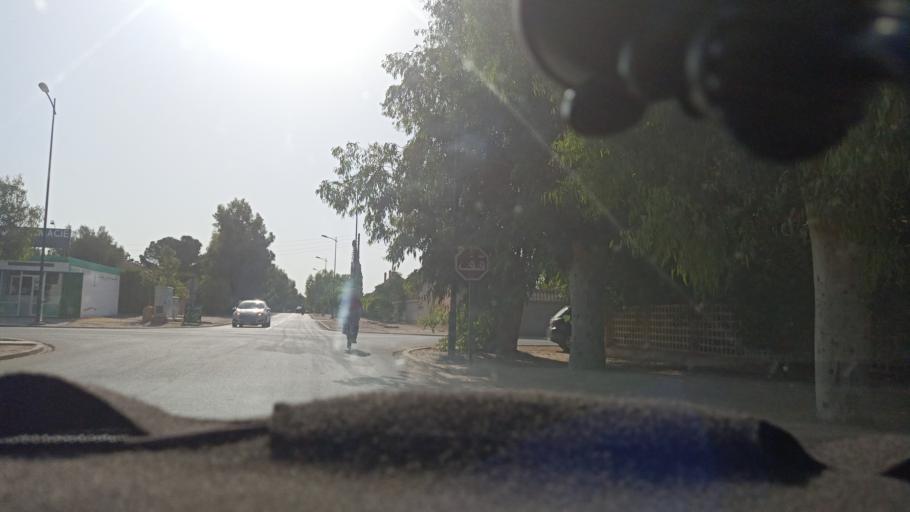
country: MA
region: Doukkala-Abda
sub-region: Safi
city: Youssoufia
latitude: 32.2464
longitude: -8.5279
